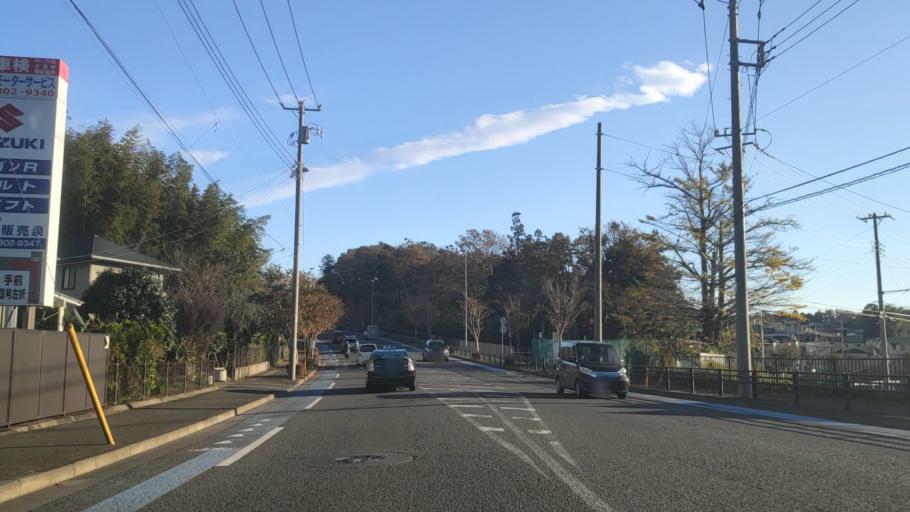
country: JP
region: Kanagawa
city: Fujisawa
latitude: 35.3961
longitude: 139.4866
